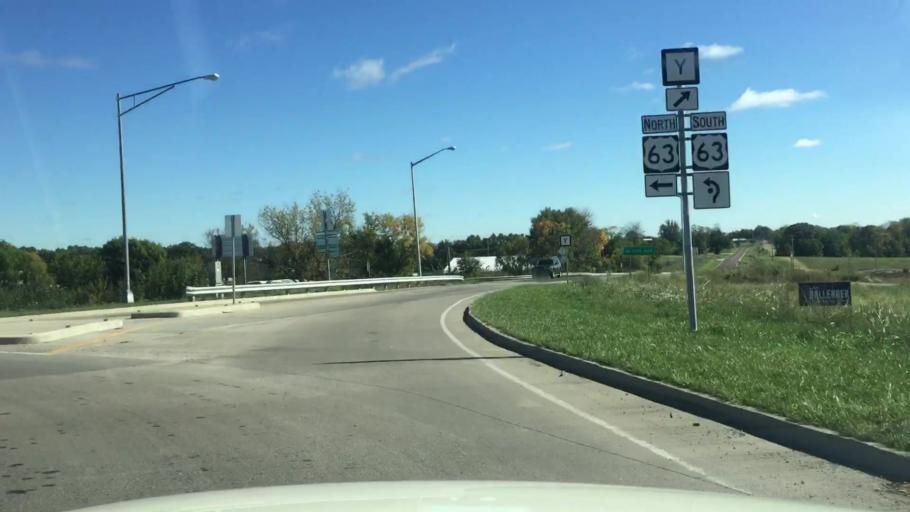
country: US
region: Missouri
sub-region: Boone County
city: Ashland
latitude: 38.7742
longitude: -92.2512
